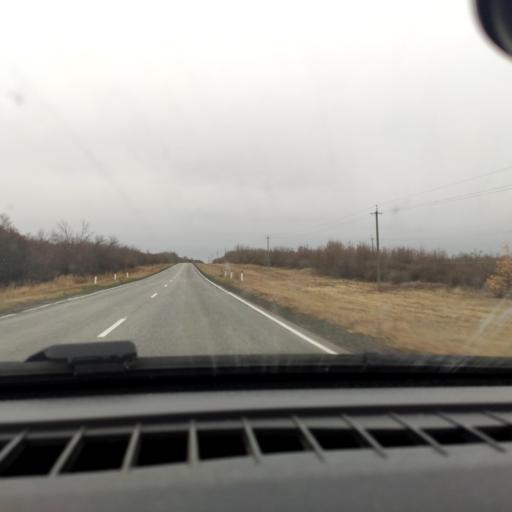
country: RU
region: Voronezj
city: Uryv-Pokrovka
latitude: 51.0936
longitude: 39.0099
